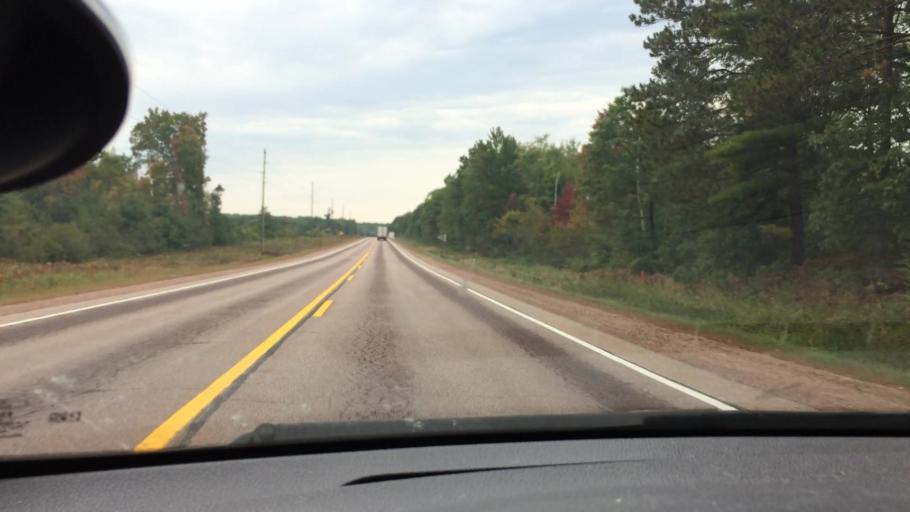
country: US
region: Wisconsin
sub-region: Clark County
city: Neillsville
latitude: 44.5871
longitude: -90.7545
